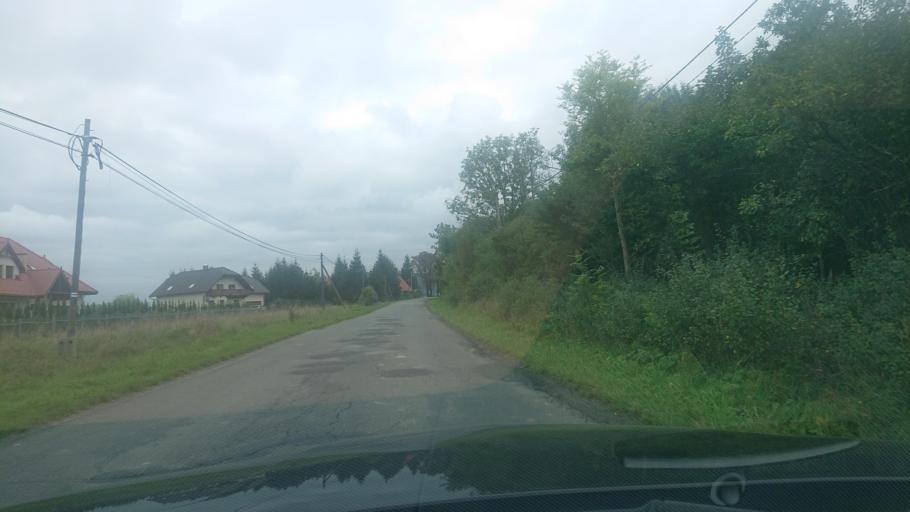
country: PL
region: Lower Silesian Voivodeship
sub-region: Powiat klodzki
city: Bystrzyca Klodzka
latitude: 50.3114
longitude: 16.6716
